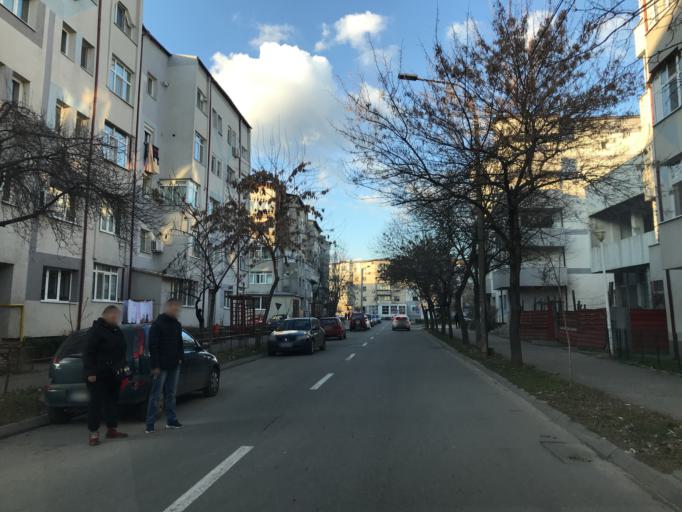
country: RO
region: Olt
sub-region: Municipiul Slatina
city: Slatina
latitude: 44.4221
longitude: 24.3816
